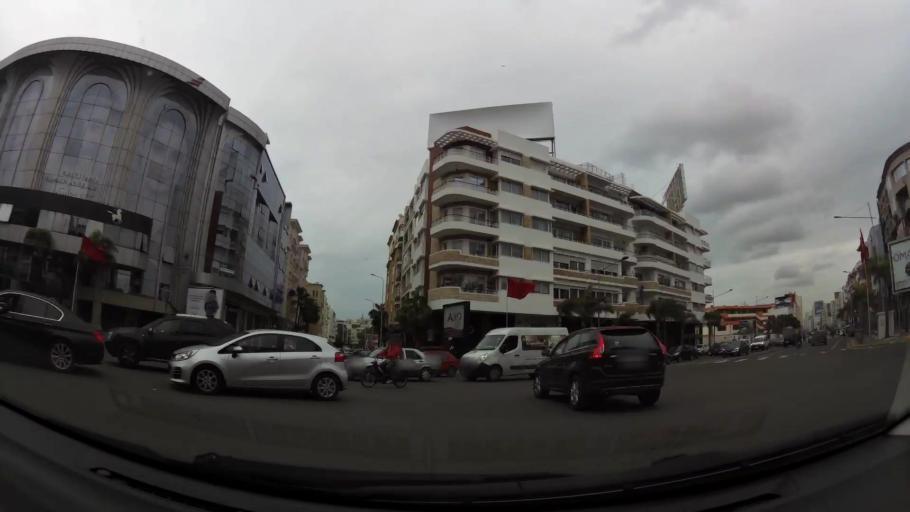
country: MA
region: Grand Casablanca
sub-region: Casablanca
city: Casablanca
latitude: 33.5880
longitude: -7.6440
